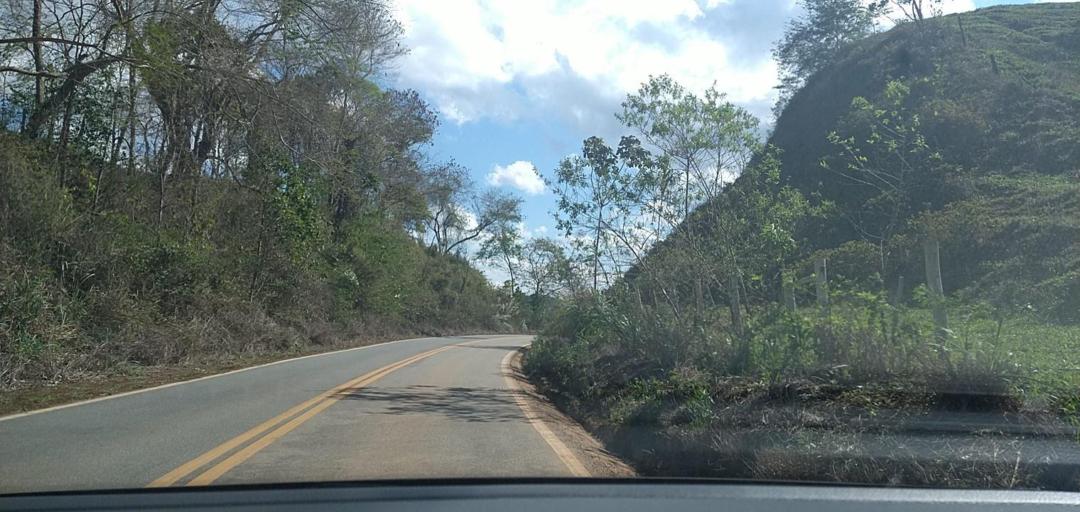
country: BR
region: Minas Gerais
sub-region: Alvinopolis
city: Alvinopolis
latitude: -20.0495
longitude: -43.0370
